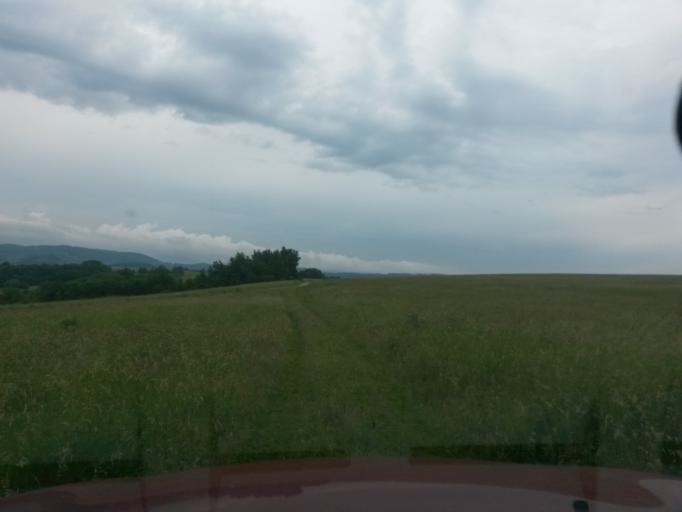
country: SK
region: Kosicky
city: Kosice
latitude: 48.7081
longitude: 21.1626
